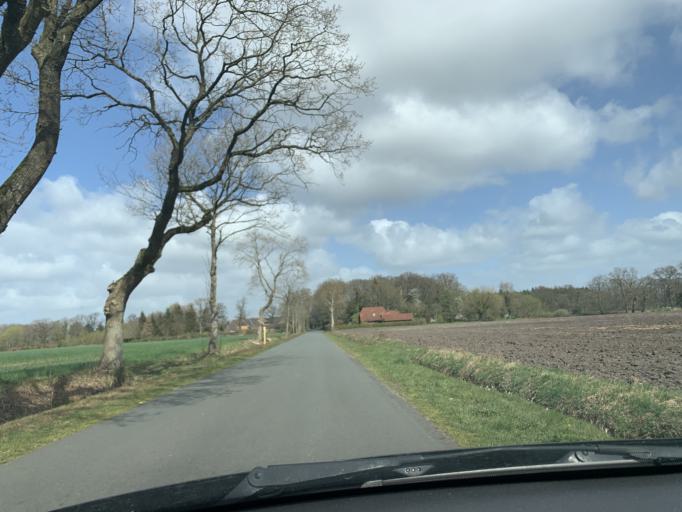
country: DE
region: Lower Saxony
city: Westerstede
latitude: 53.2796
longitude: 7.9429
